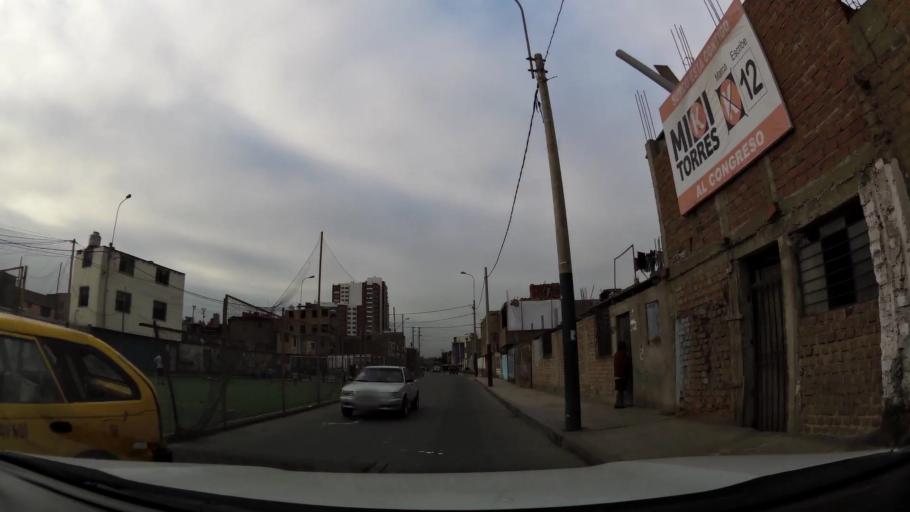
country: PE
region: Lima
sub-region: Lima
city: Surco
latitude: -12.1464
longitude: -77.0105
